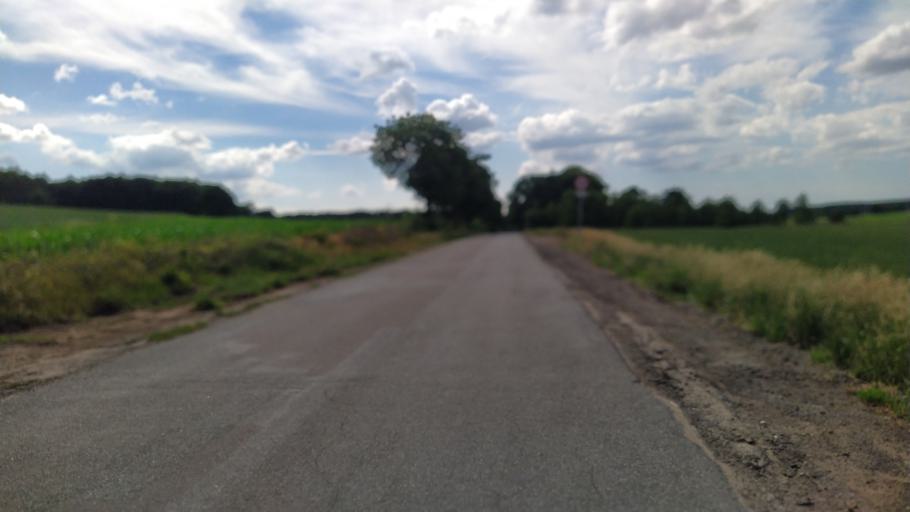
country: DE
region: Lower Saxony
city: Armstorf
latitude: 53.6060
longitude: 9.0577
